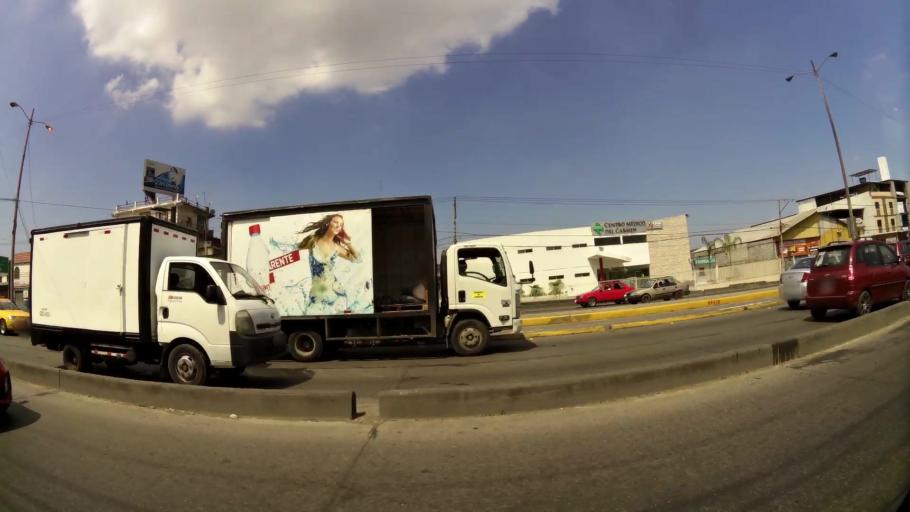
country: EC
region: Guayas
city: Guayaquil
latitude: -2.1255
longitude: -79.9314
